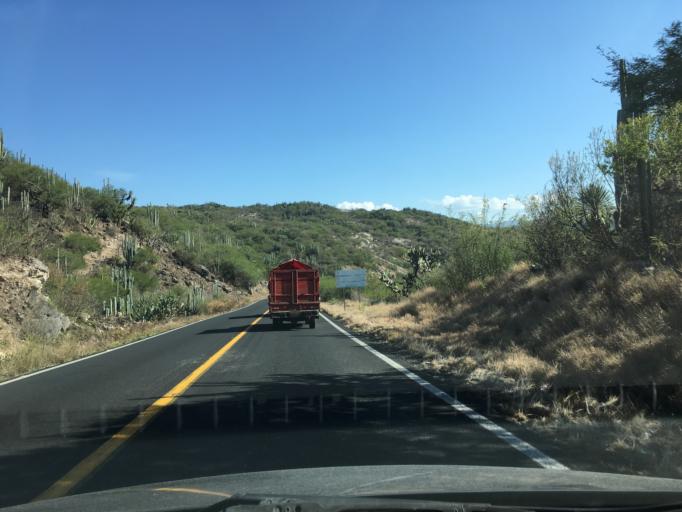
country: MX
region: Hidalgo
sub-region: San Agustin Metzquititlan
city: Mezquititlan
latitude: 20.4586
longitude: -98.6788
